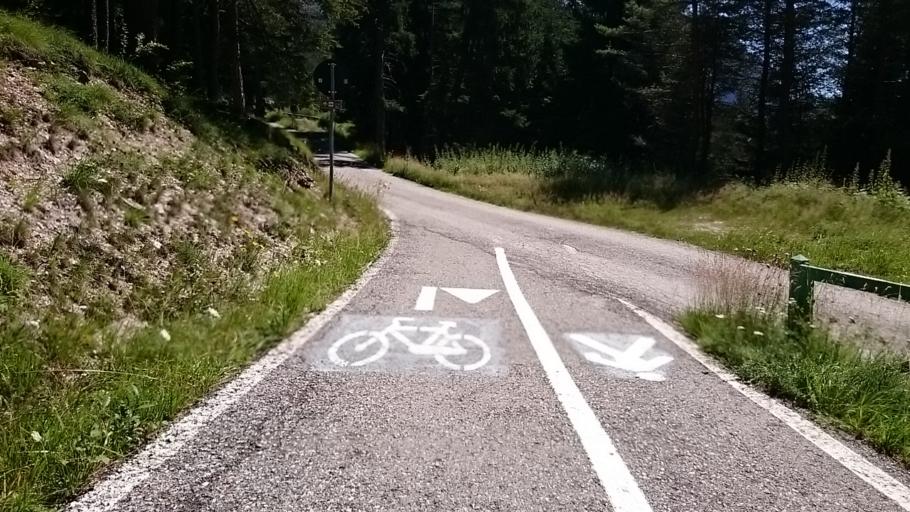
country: IT
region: Veneto
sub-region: Provincia di Belluno
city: San Vito
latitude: 46.4869
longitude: 12.1891
